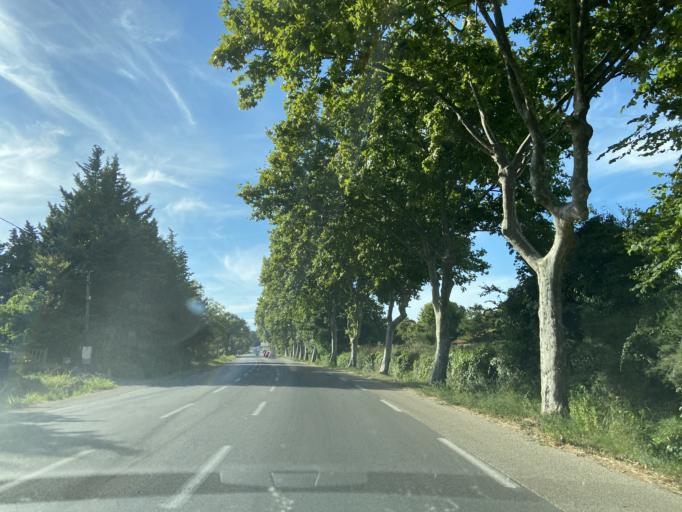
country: FR
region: Provence-Alpes-Cote d'Azur
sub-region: Departement des Bouches-du-Rhone
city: Miramas
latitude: 43.5742
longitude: 5.0176
